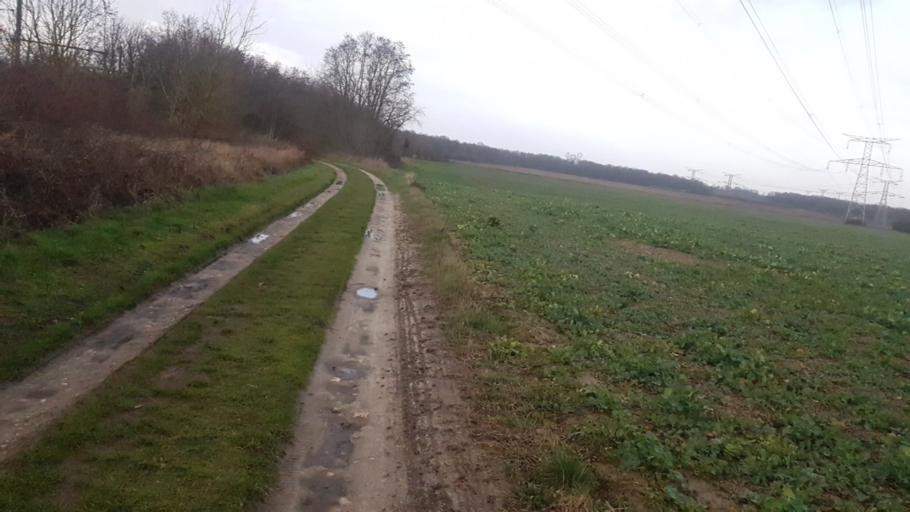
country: FR
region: Ile-de-France
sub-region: Departement de l'Essonne
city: Cheptainville
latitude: 48.5397
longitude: 2.2938
